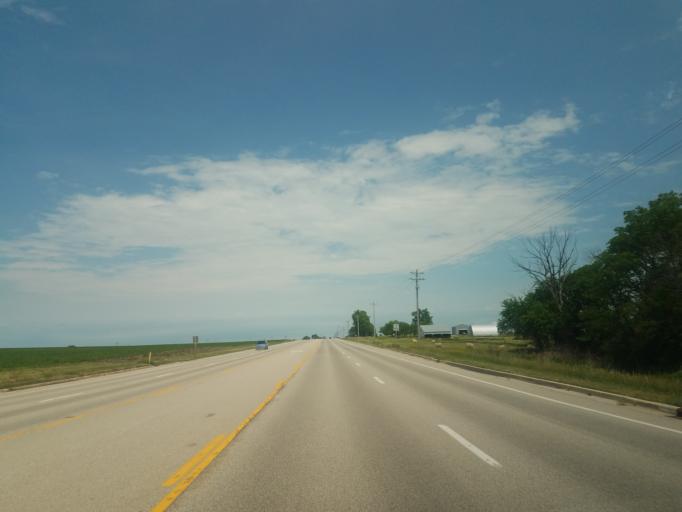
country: US
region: Illinois
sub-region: McLean County
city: Downs
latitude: 40.4257
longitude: -88.9012
